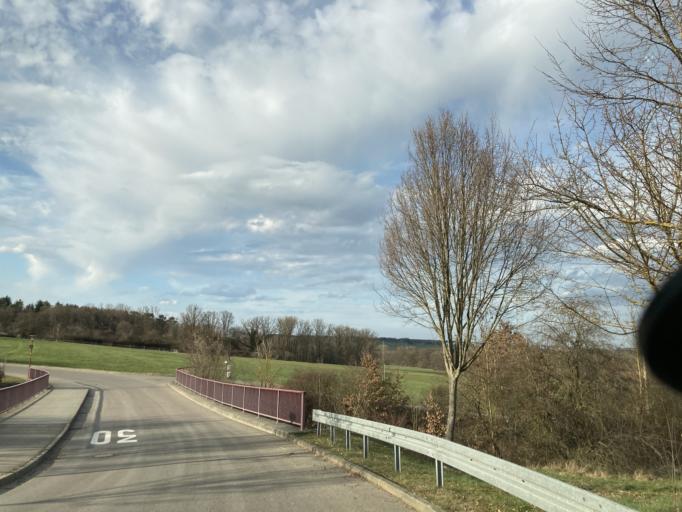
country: DE
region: Baden-Wuerttemberg
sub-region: Tuebingen Region
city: Dusslingen
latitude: 48.4504
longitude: 9.0691
